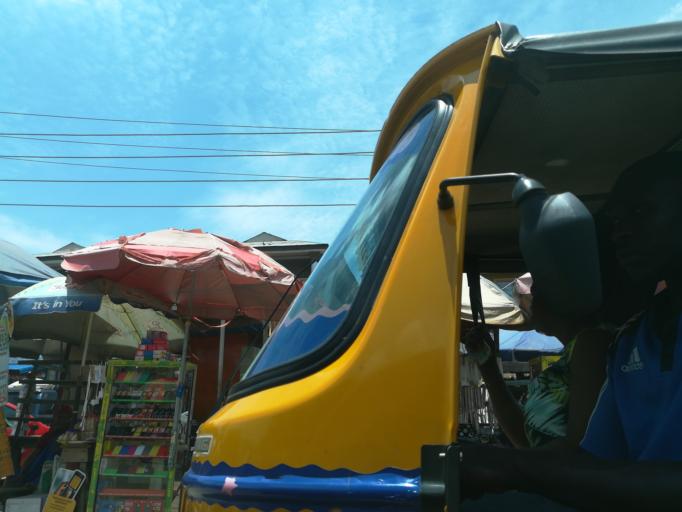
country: NG
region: Lagos
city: Ikorodu
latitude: 6.6189
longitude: 3.5032
